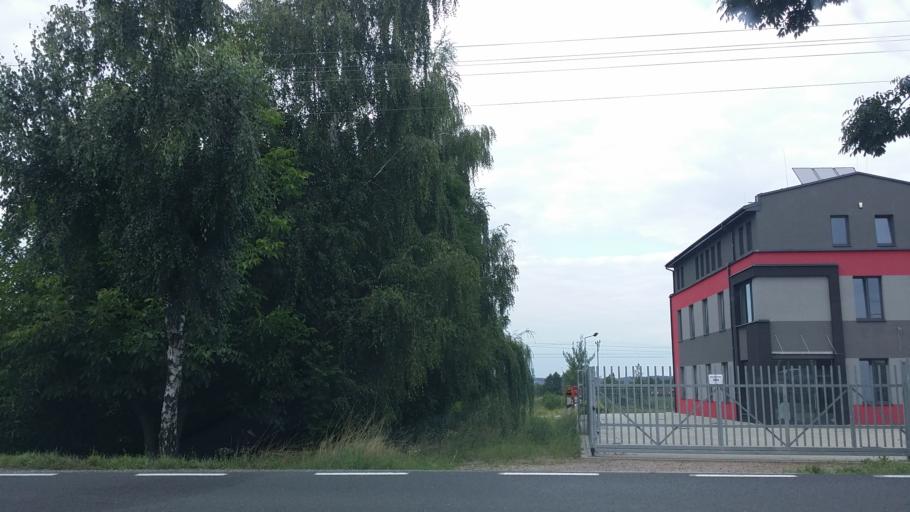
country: PL
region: Lesser Poland Voivodeship
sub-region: Powiat krakowski
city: Krzecin
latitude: 49.9589
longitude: 19.7285
